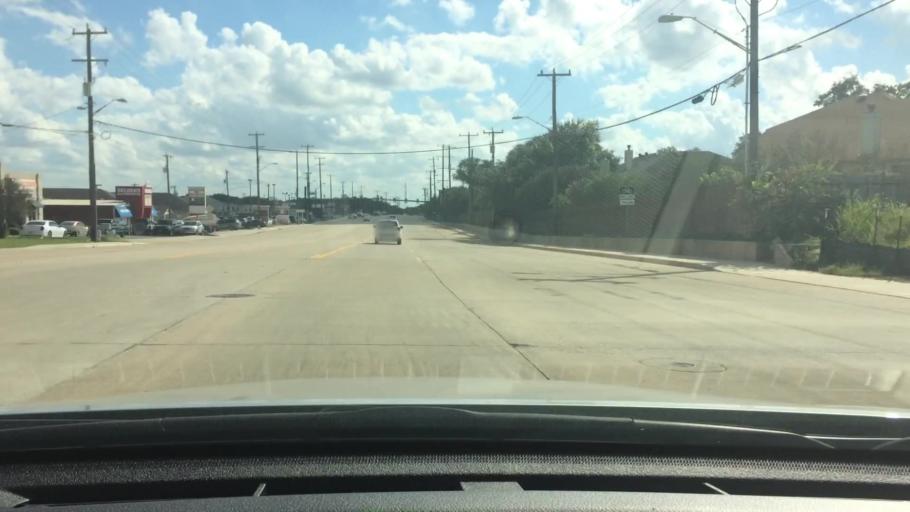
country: US
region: Texas
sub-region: Bexar County
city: Hollywood Park
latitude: 29.6459
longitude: -98.4252
